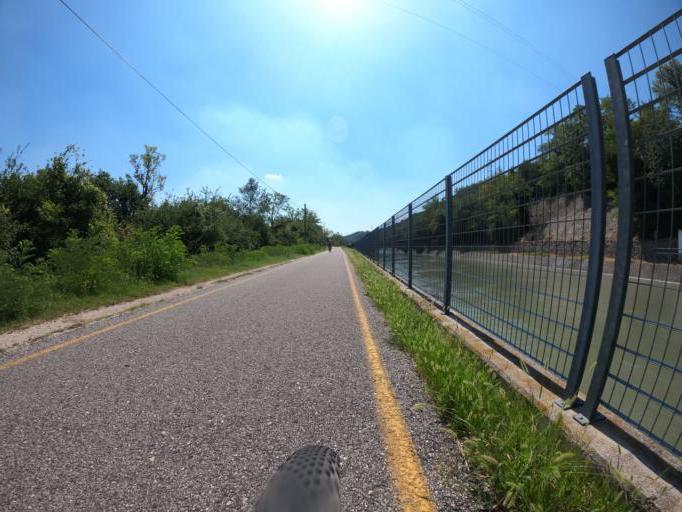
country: IT
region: Veneto
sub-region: Provincia di Verona
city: Volargne
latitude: 45.5236
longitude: 10.7975
